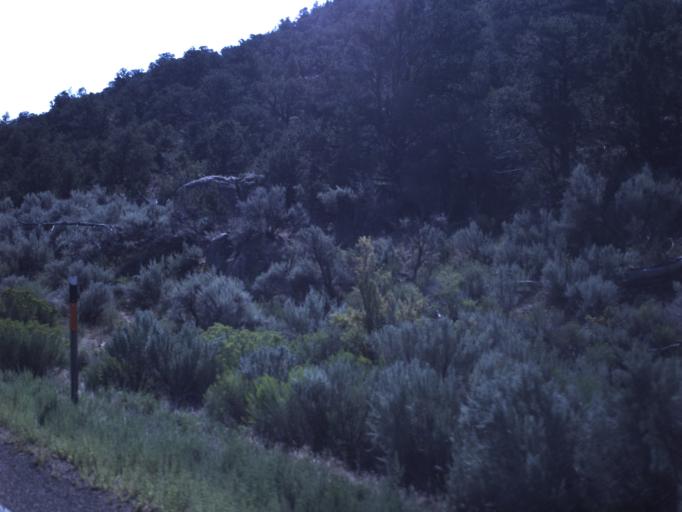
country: US
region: Utah
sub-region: Duchesne County
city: Duchesne
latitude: 40.2963
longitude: -110.5864
